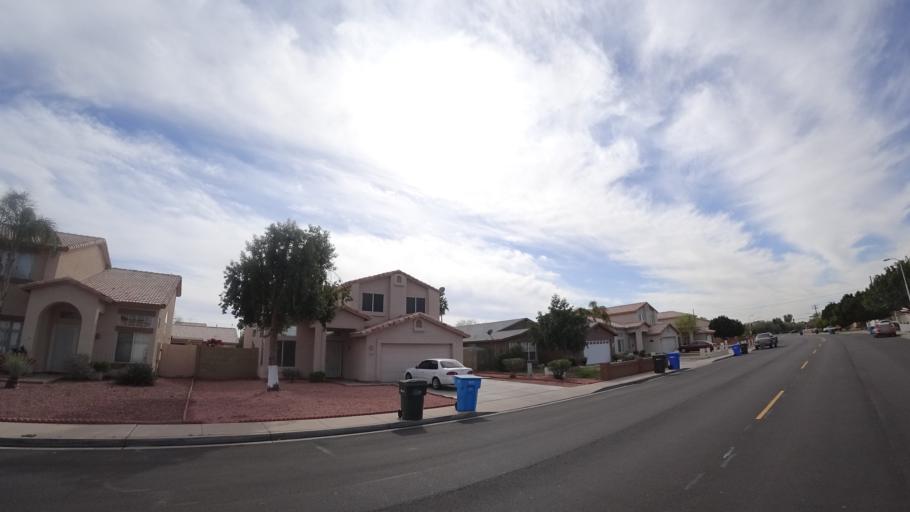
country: US
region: Arizona
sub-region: Maricopa County
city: Tolleson
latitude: 33.4724
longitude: -112.2531
